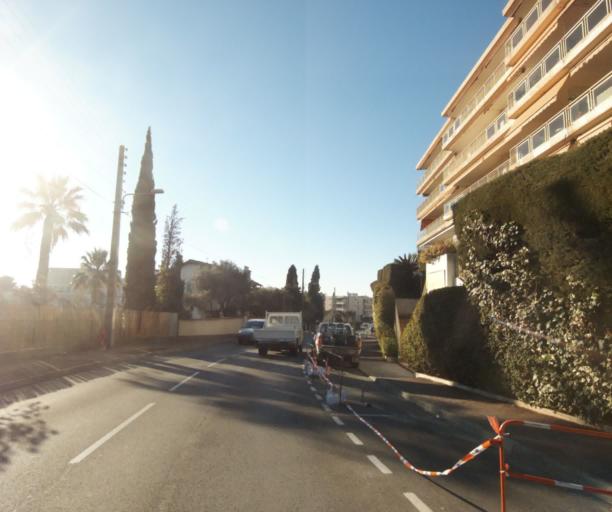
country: FR
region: Provence-Alpes-Cote d'Azur
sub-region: Departement des Alpes-Maritimes
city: Antibes
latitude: 43.5824
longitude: 7.1100
